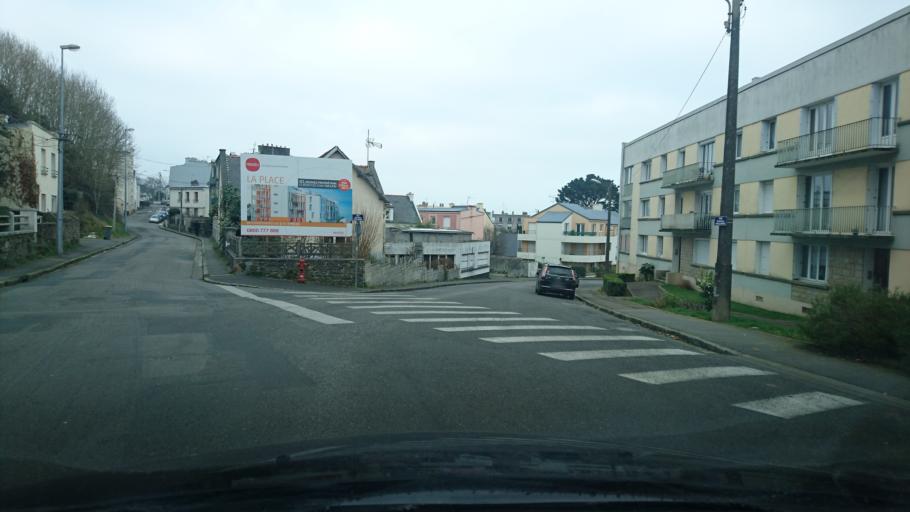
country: FR
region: Brittany
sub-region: Departement du Finistere
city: Brest
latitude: 48.3849
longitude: -4.5115
